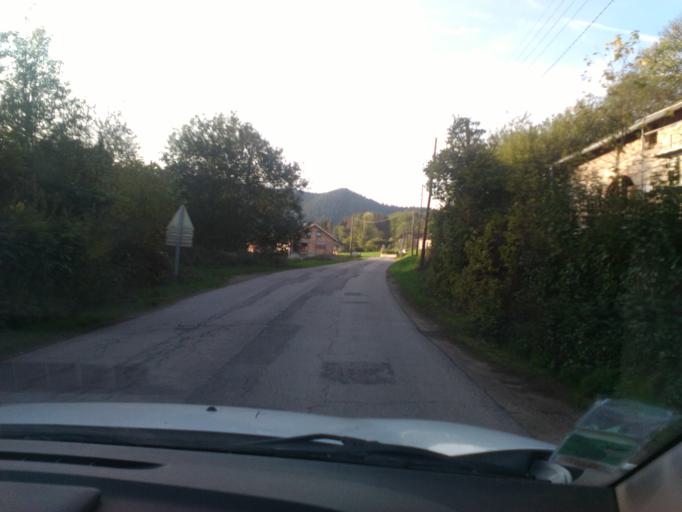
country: FR
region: Lorraine
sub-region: Departement des Vosges
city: Taintrux
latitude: 48.2488
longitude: 6.9065
